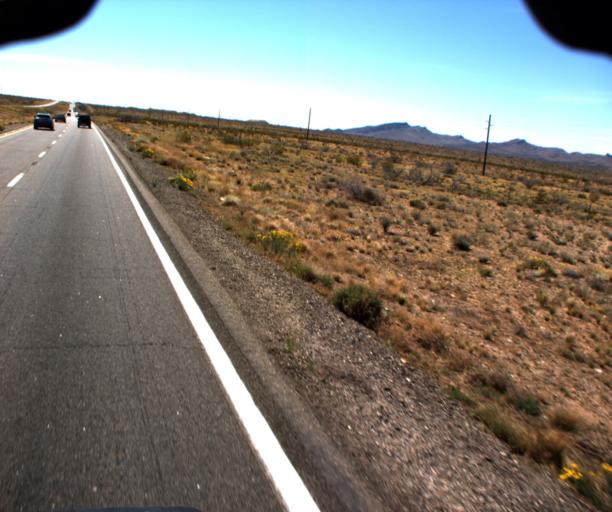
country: US
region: Arizona
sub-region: Mohave County
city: Dolan Springs
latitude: 35.4380
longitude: -114.2893
